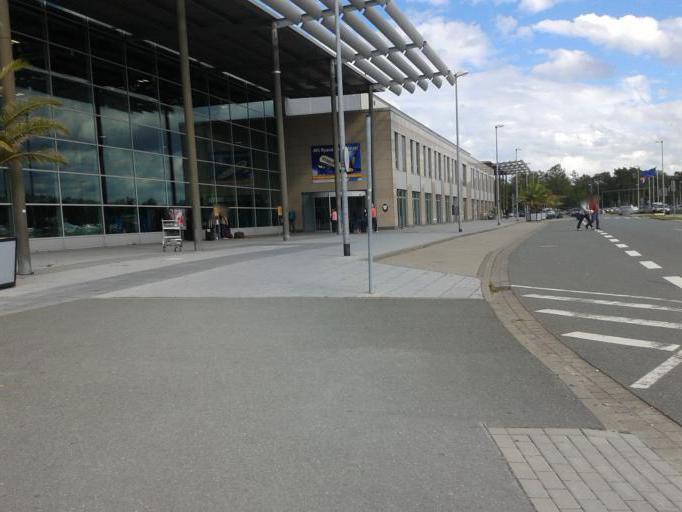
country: DE
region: North Rhine-Westphalia
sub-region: Regierungsbezirk Dusseldorf
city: Weeze
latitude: 51.5991
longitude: 6.1492
